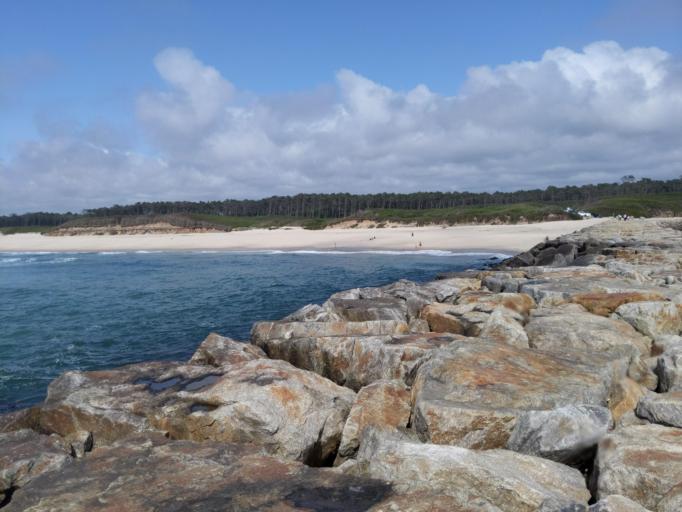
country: PT
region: Aveiro
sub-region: Ovar
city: Esmoriz
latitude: 40.9313
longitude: -8.6619
